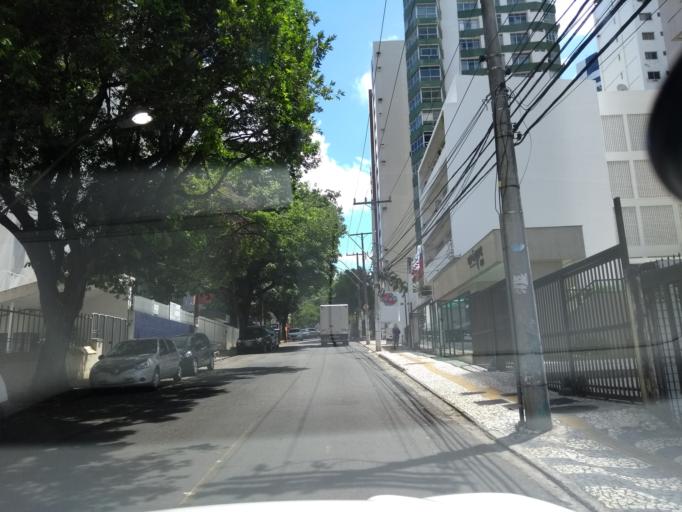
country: BR
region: Bahia
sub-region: Salvador
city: Salvador
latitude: -12.9967
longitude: -38.5181
